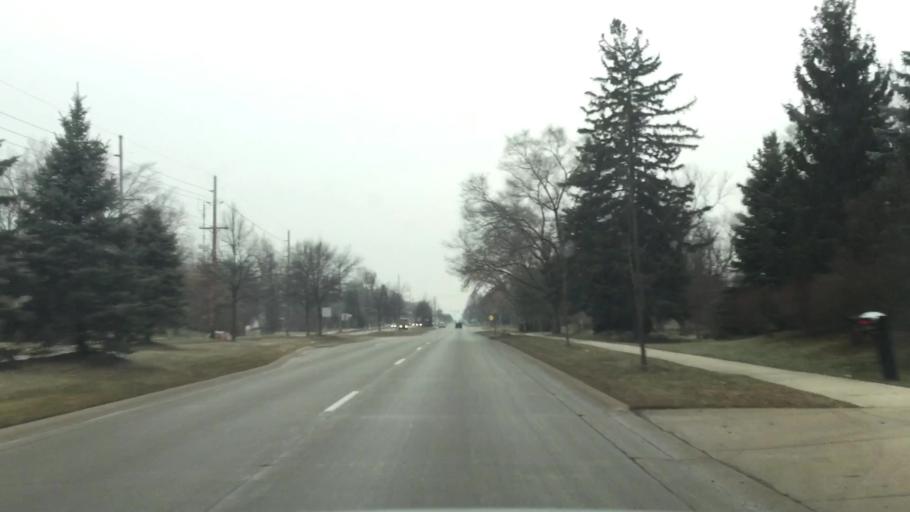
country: US
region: Michigan
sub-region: Oakland County
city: Farmington Hills
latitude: 42.4793
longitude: -83.3575
